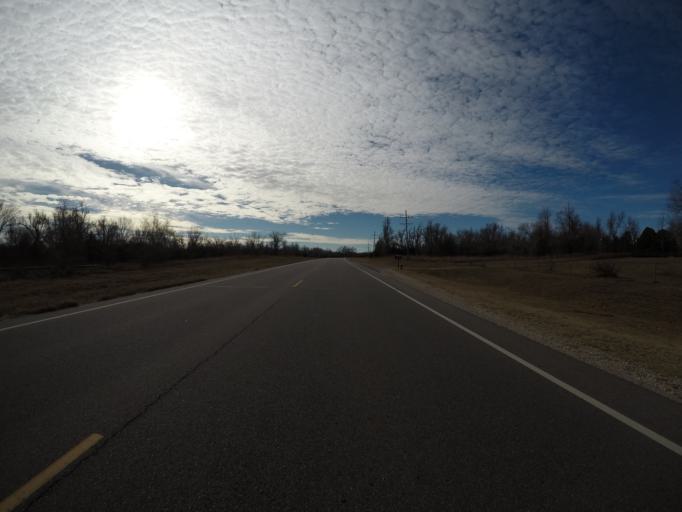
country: US
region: Kansas
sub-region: Reno County
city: Hutchinson
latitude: 38.1136
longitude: -97.8650
